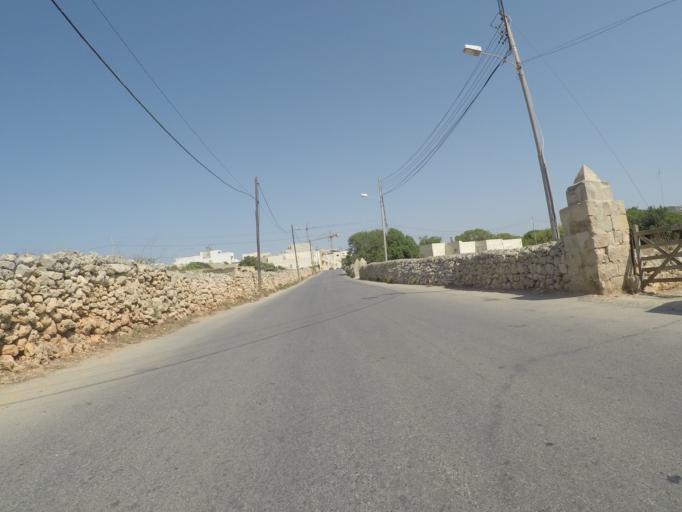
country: MT
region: L-Imgarr
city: Imgarr
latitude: 35.9211
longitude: 14.3598
